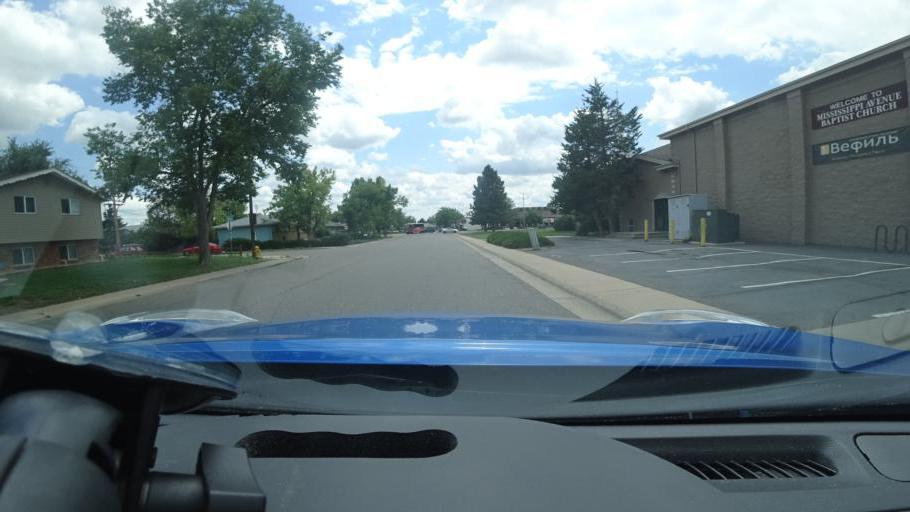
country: US
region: Colorado
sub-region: Adams County
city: Aurora
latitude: 39.6976
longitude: -104.8351
